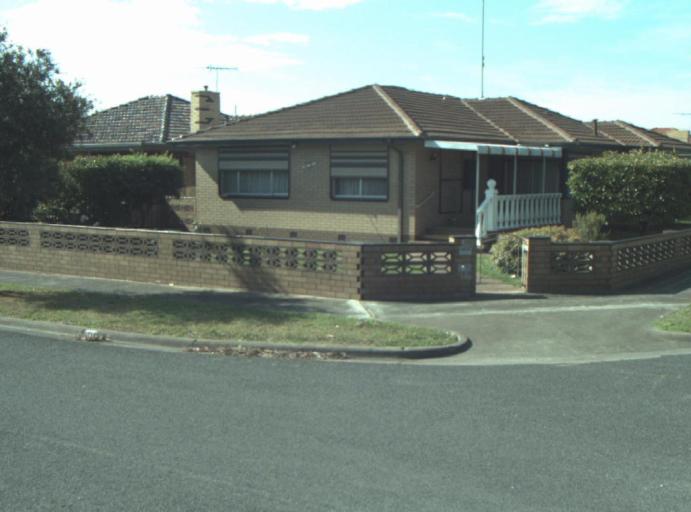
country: AU
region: Victoria
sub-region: Greater Geelong
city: Bell Park
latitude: -38.1070
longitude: 144.3381
